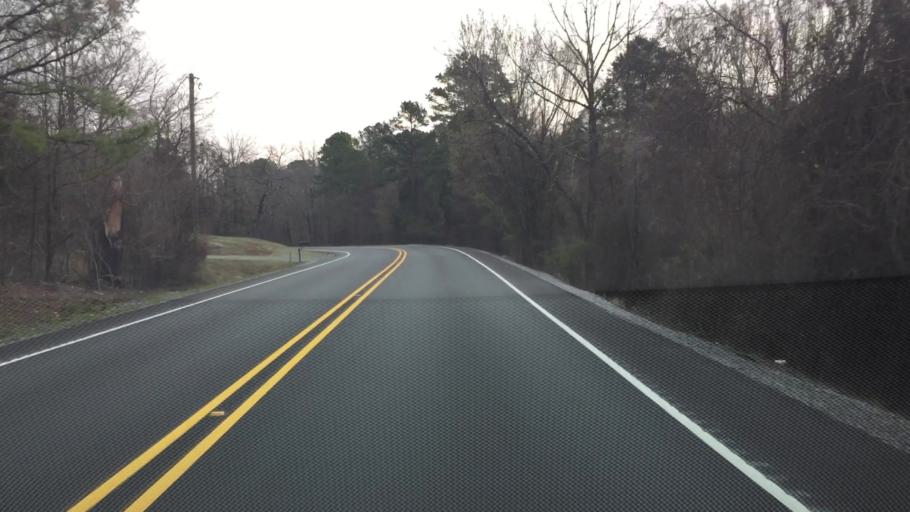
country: US
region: Arkansas
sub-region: Saline County
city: Haskell
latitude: 34.6117
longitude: -92.8019
